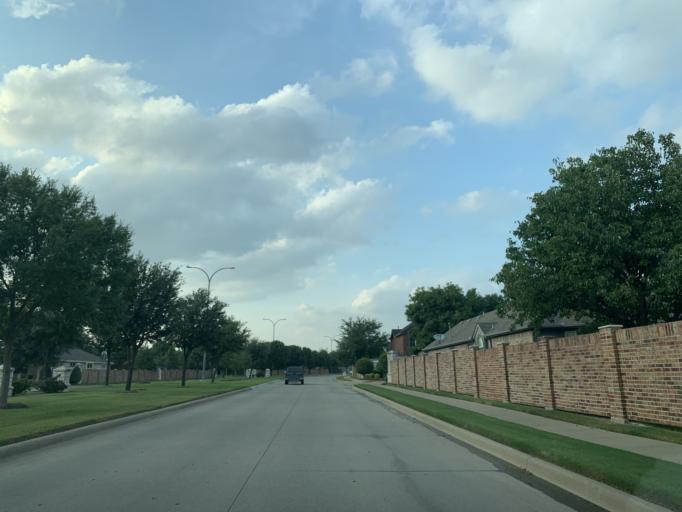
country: US
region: Texas
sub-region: Tarrant County
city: Keller
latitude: 32.9396
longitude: -97.2724
